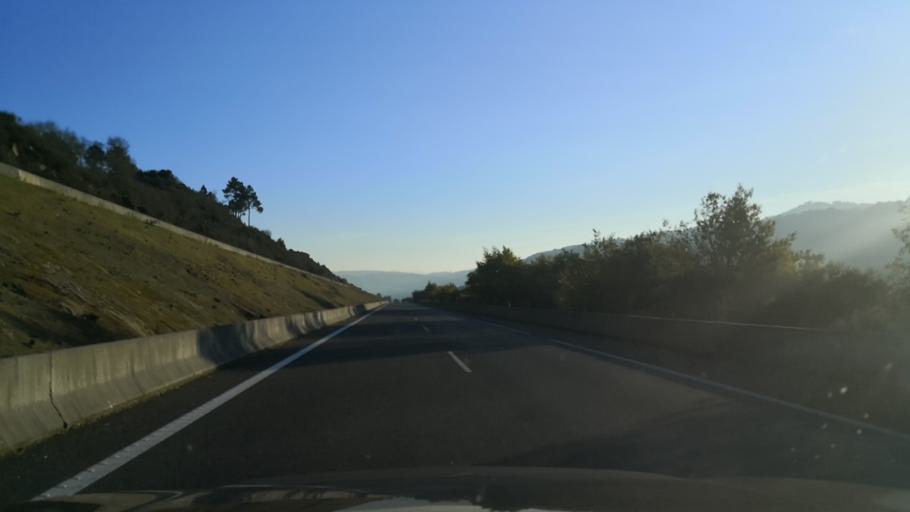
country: ES
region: Galicia
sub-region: Provincia de Ourense
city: Punxin
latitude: 42.3705
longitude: -7.9935
